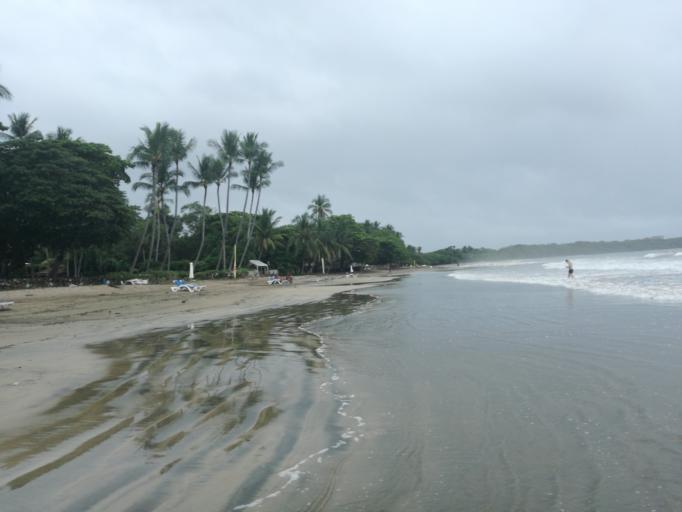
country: CR
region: Guanacaste
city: Santa Cruz
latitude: 10.3014
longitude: -85.8414
